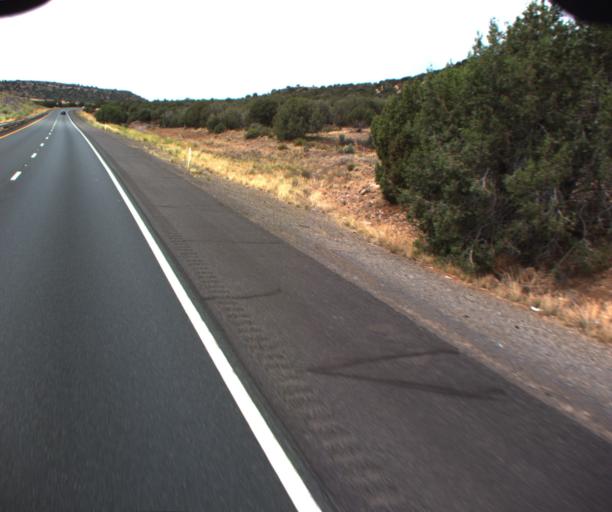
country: US
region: Arizona
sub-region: Yavapai County
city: Camp Verde
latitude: 34.4977
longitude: -112.0047
